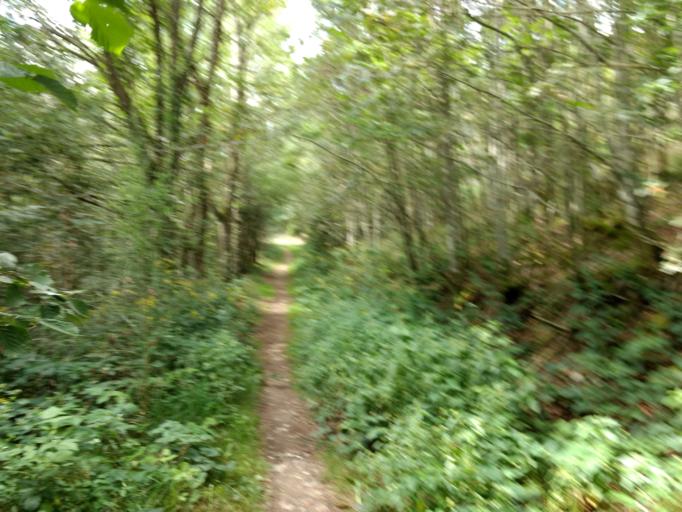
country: BE
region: Wallonia
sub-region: Province du Luxembourg
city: Houffalize
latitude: 50.1429
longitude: 5.7342
